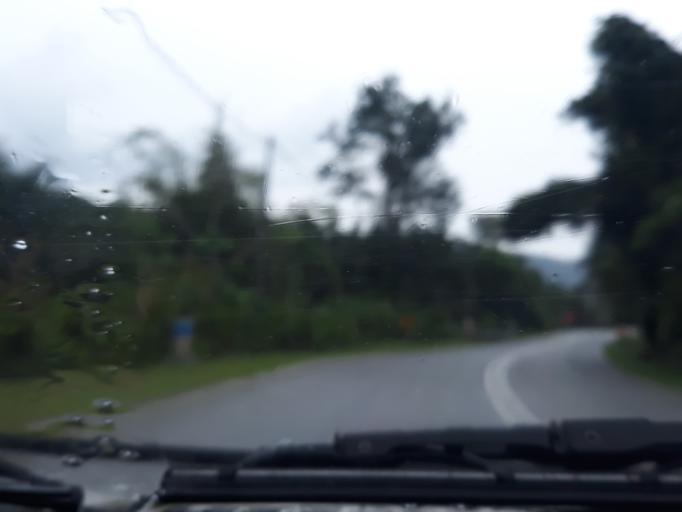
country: MY
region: Kedah
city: Kulim
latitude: 5.2814
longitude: 100.6224
